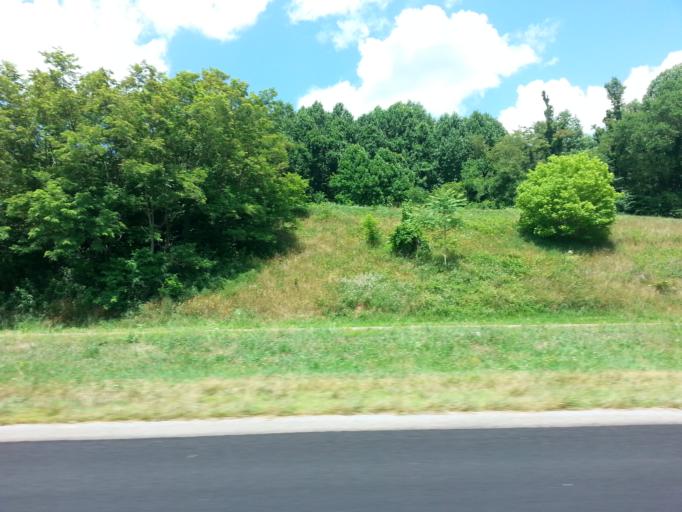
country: US
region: Virginia
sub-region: Lee County
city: Jonesville
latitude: 36.6931
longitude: -83.2366
